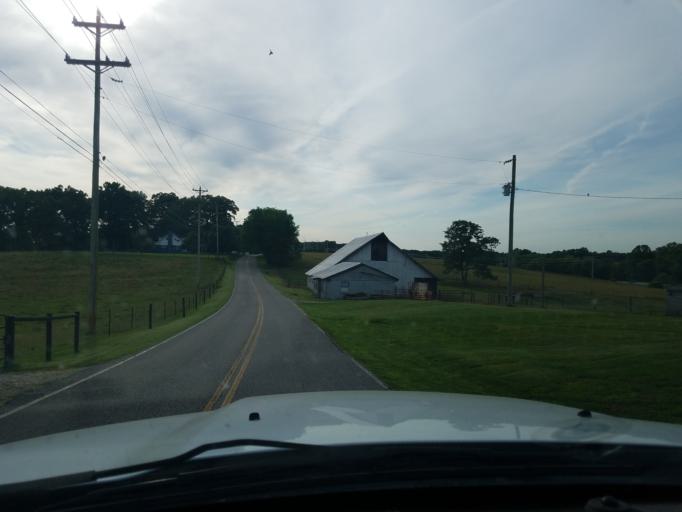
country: US
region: Tennessee
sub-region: Putnam County
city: Baxter
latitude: 36.1322
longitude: -85.5754
